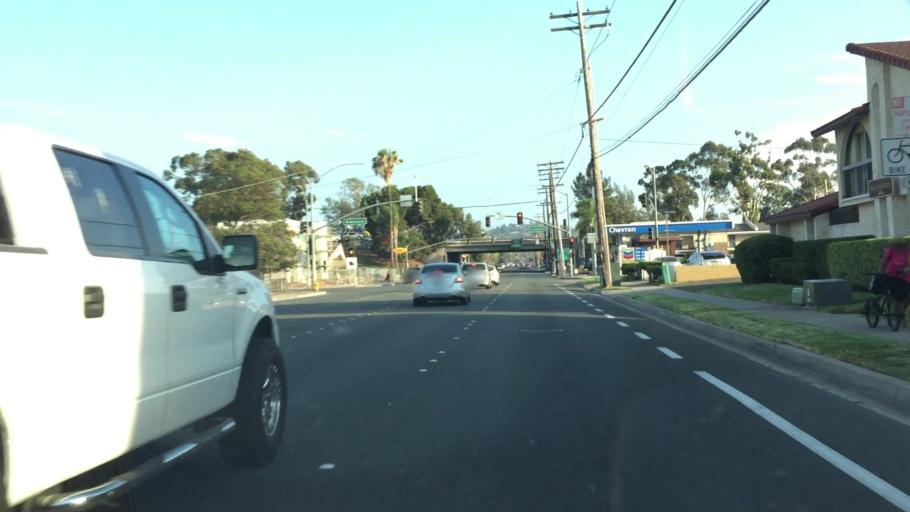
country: US
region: California
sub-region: San Diego County
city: Bostonia
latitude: 32.8050
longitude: -116.9511
